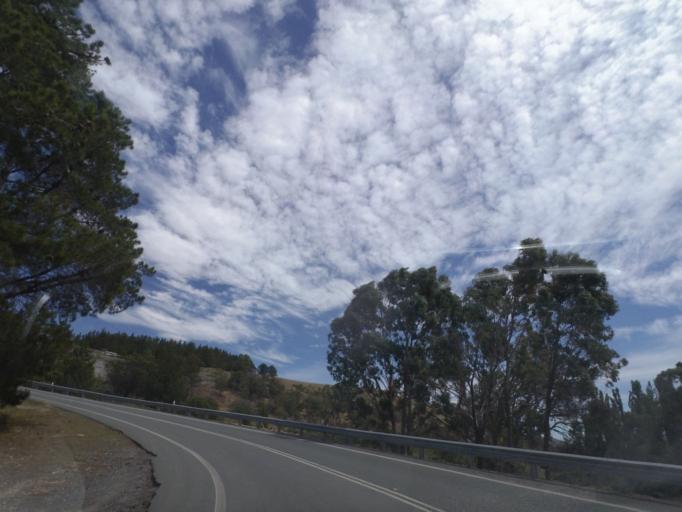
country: AU
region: New South Wales
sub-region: Yass Valley
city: Gundaroo
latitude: -35.1001
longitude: 149.3764
